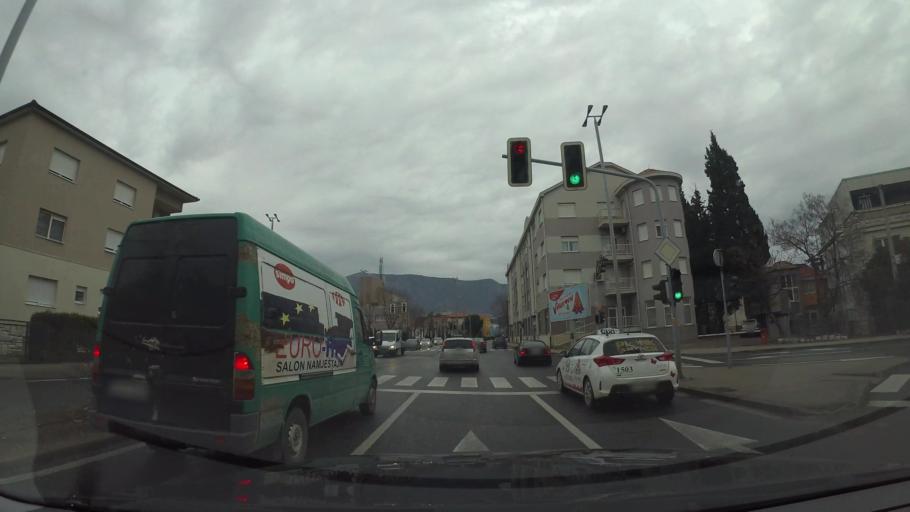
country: BA
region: Federation of Bosnia and Herzegovina
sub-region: Hercegovacko-Bosanski Kanton
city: Mostar
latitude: 43.3396
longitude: 17.8091
